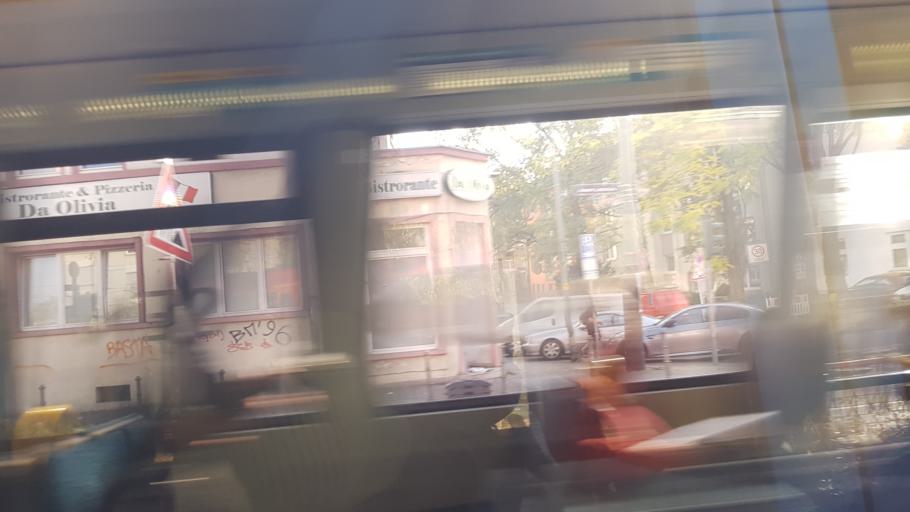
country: DE
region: Hesse
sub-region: Regierungsbezirk Darmstadt
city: Frankfurt am Main
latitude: 50.1129
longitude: 8.7006
